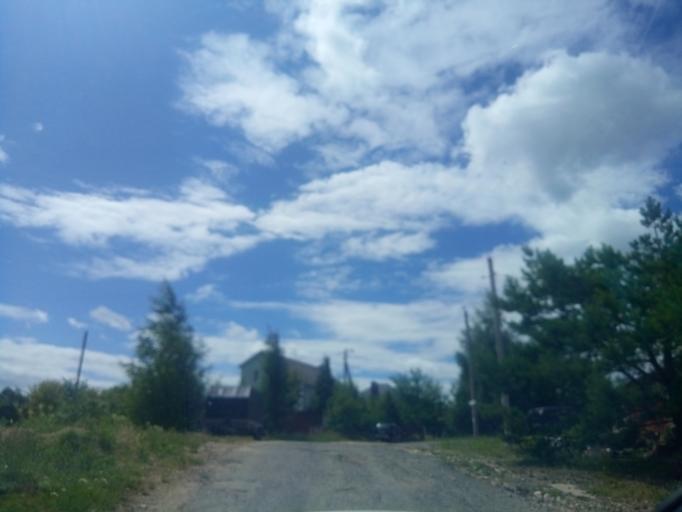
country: BY
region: Minsk
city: Zhdanovichy
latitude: 53.9379
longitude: 27.4102
